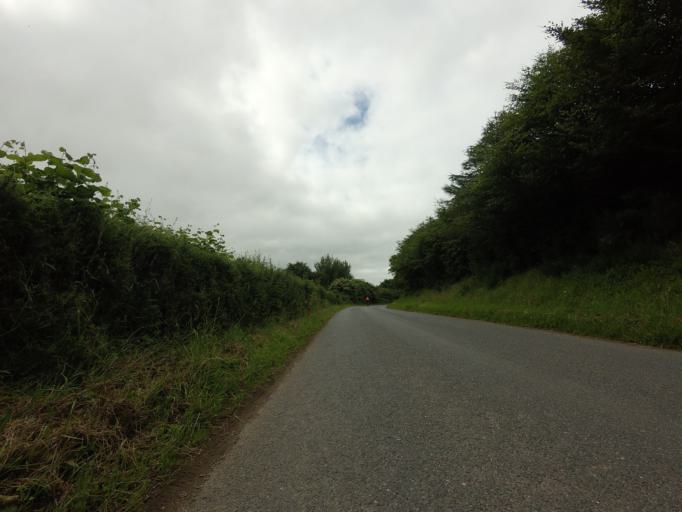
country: GB
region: Scotland
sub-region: Aberdeenshire
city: Rosehearty
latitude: 57.5370
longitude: -2.1862
